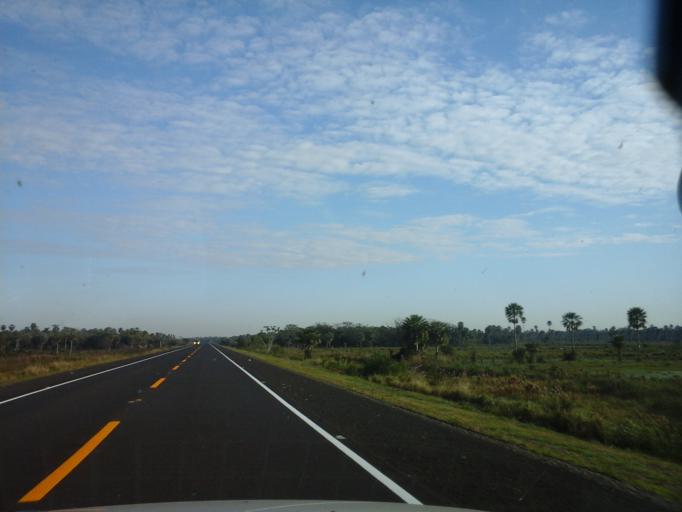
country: PY
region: Neembucu
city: Cerrito
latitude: -26.8752
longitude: -57.7494
